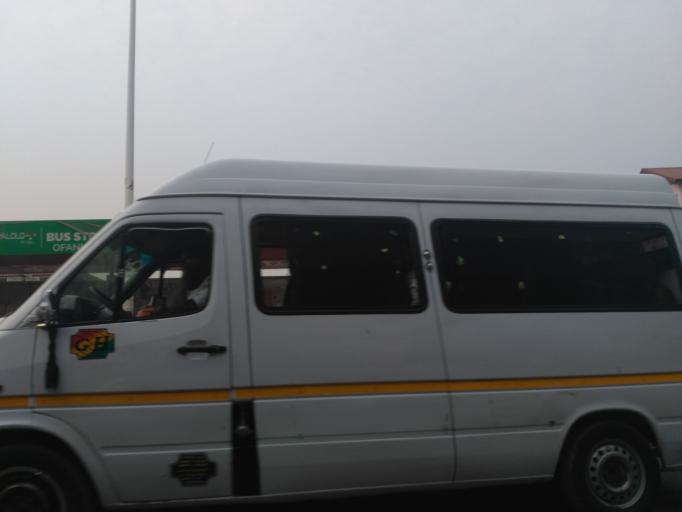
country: GH
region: Greater Accra
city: Dome
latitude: 5.6578
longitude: -0.2656
